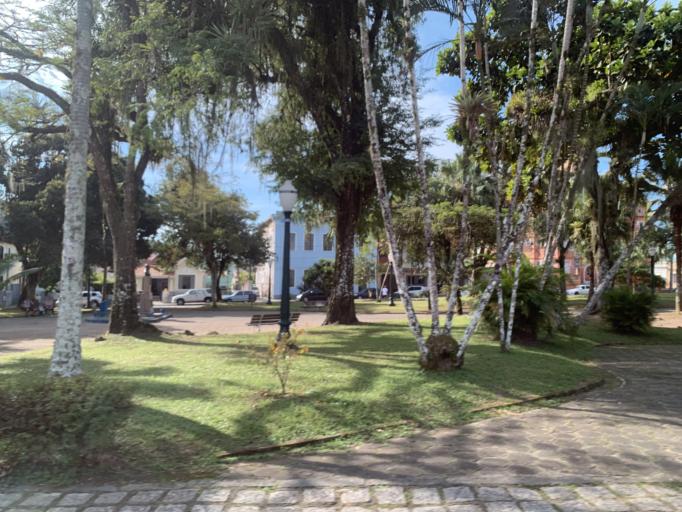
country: BR
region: Parana
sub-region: Antonina
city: Antonina
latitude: -25.4313
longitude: -48.7114
